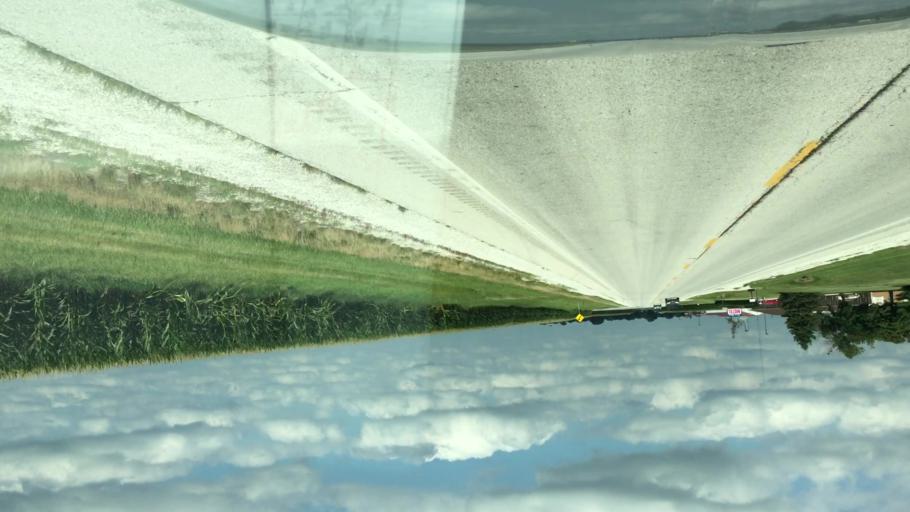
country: US
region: Illinois
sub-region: Hancock County
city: Carthage
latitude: 40.4080
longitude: -91.1698
